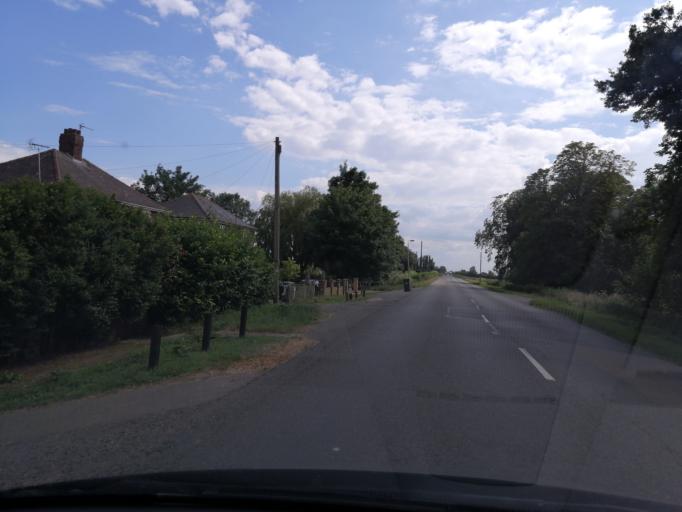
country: GB
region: England
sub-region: Cambridgeshire
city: Whittlesey
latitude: 52.5064
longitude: -0.1445
